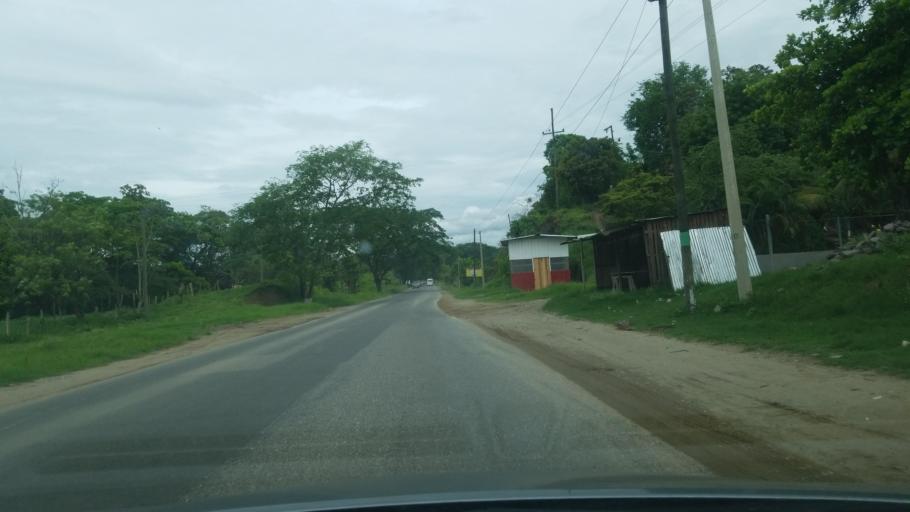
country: HN
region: Santa Barbara
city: La Flecha
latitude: 15.2964
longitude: -88.4625
